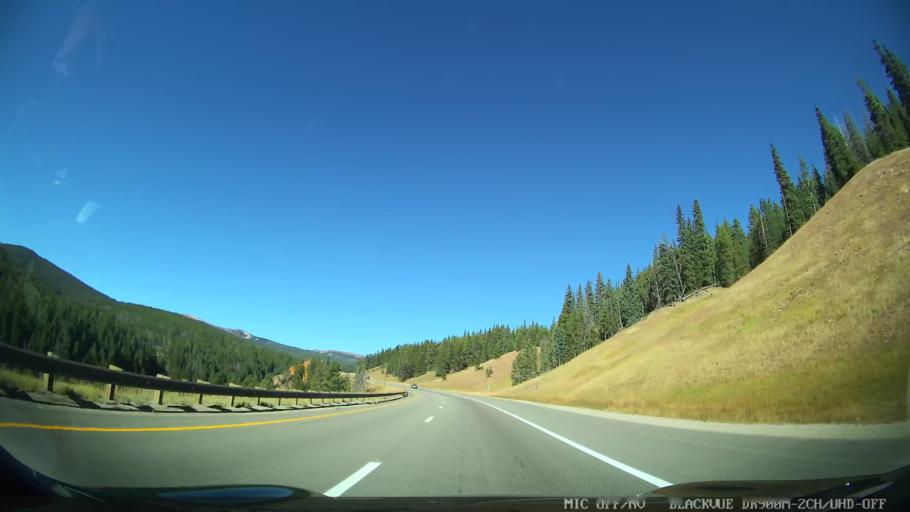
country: US
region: Colorado
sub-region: Summit County
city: Frisco
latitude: 39.5032
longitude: -106.1717
